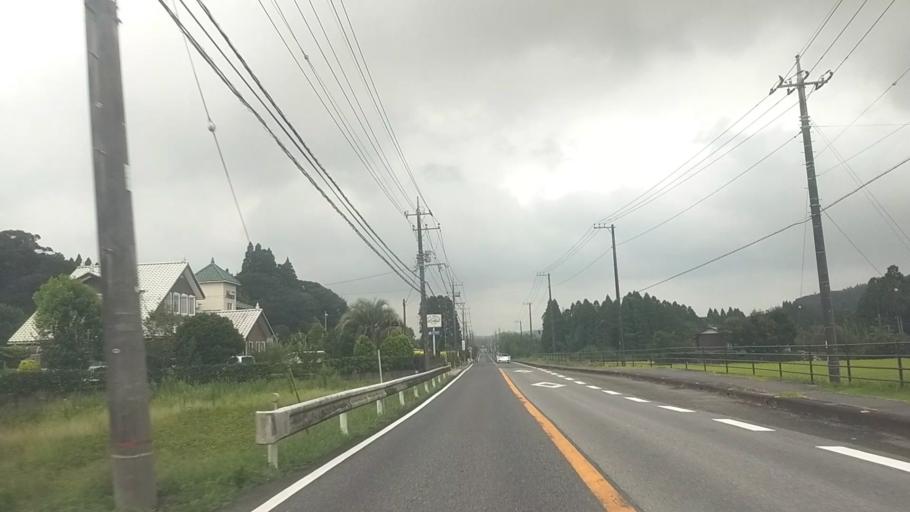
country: JP
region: Chiba
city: Ohara
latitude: 35.2844
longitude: 140.2715
